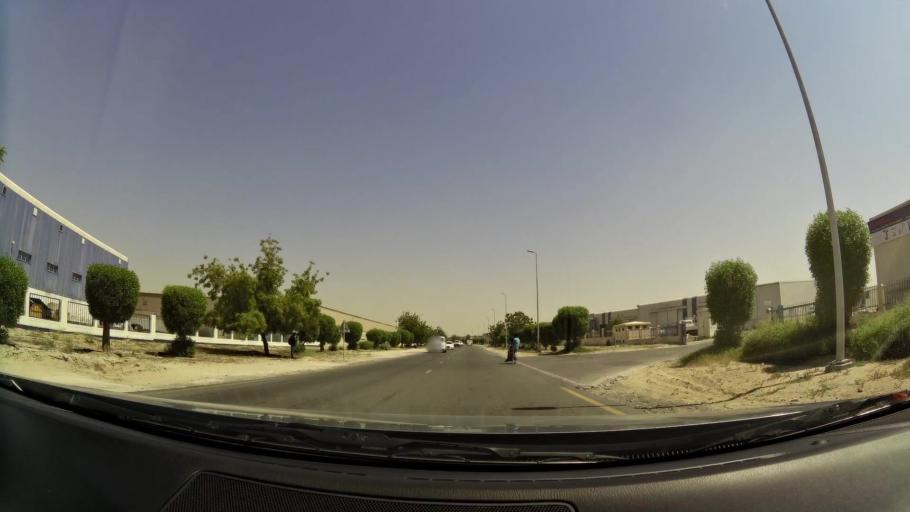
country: AE
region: Dubai
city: Dubai
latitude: 24.9898
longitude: 55.1548
